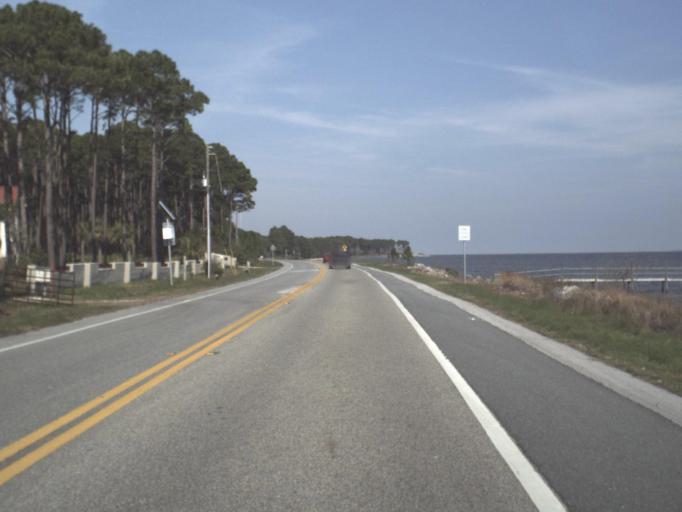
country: US
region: Florida
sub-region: Franklin County
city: Eastpoint
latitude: 29.7631
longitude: -84.8140
